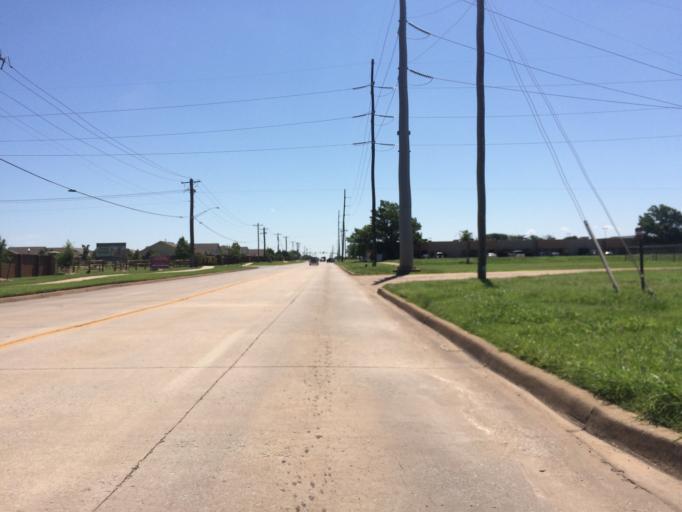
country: US
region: Oklahoma
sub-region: Cleveland County
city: Norman
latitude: 35.2474
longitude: -97.4553
